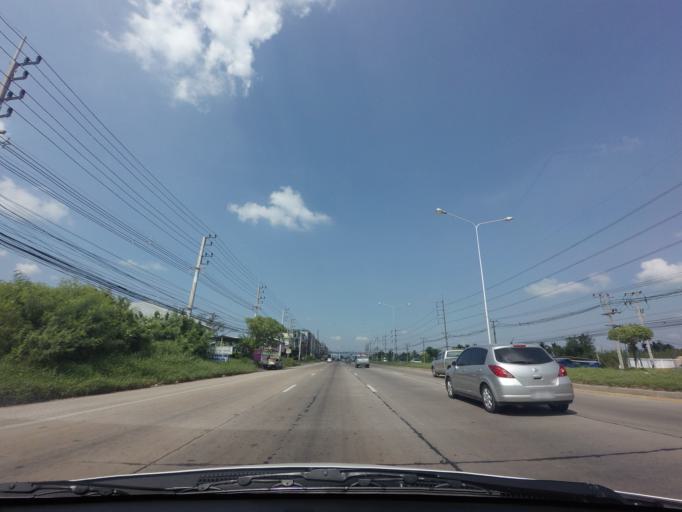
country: TH
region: Nakhon Pathom
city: Sam Phran
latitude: 13.7548
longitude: 100.1929
